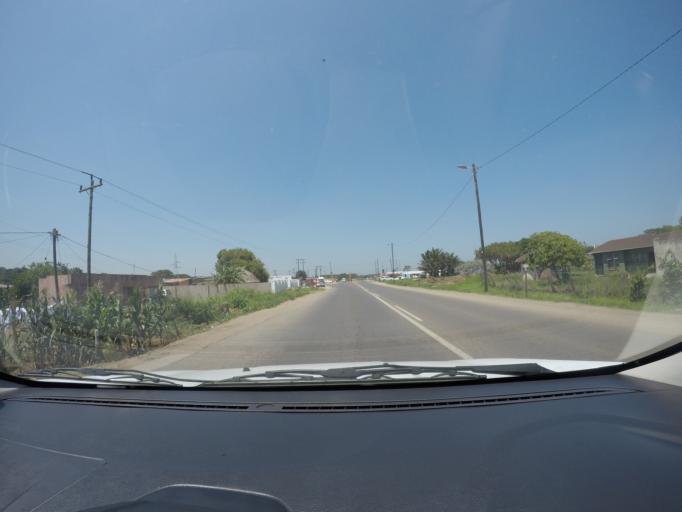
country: ZA
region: KwaZulu-Natal
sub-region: uThungulu District Municipality
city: eSikhawini
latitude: -28.8584
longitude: 31.9224
